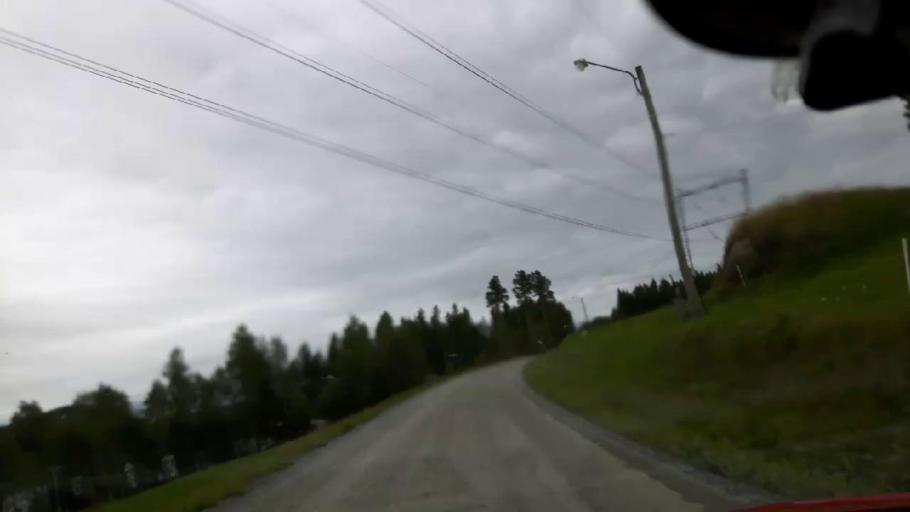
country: SE
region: Jaemtland
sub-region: Braecke Kommun
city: Braecke
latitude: 63.0808
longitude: 15.2846
